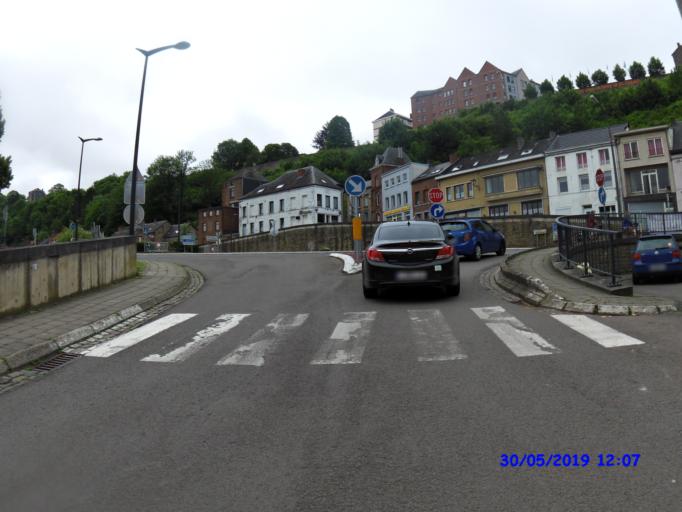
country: BE
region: Wallonia
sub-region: Province du Hainaut
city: Thuin
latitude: 50.3409
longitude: 4.2867
